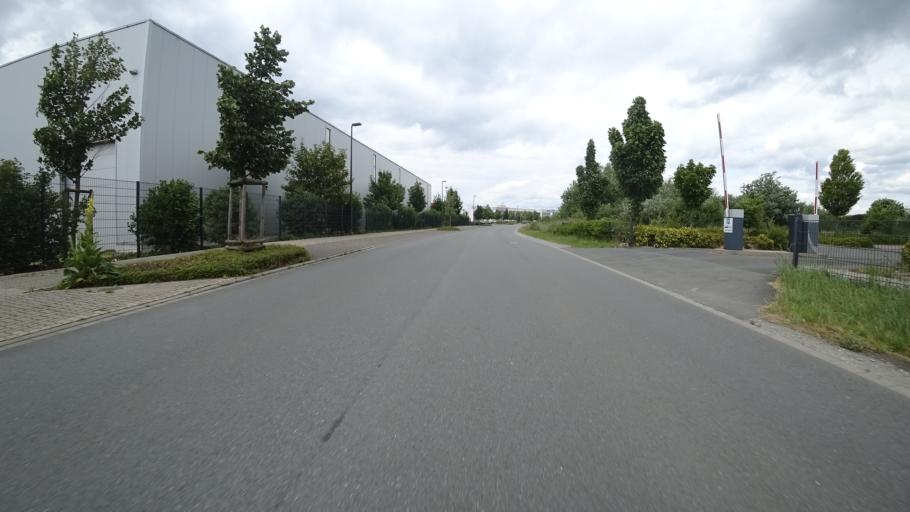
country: DE
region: North Rhine-Westphalia
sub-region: Regierungsbezirk Arnsberg
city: Lippstadt
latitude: 51.6485
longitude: 8.3512
